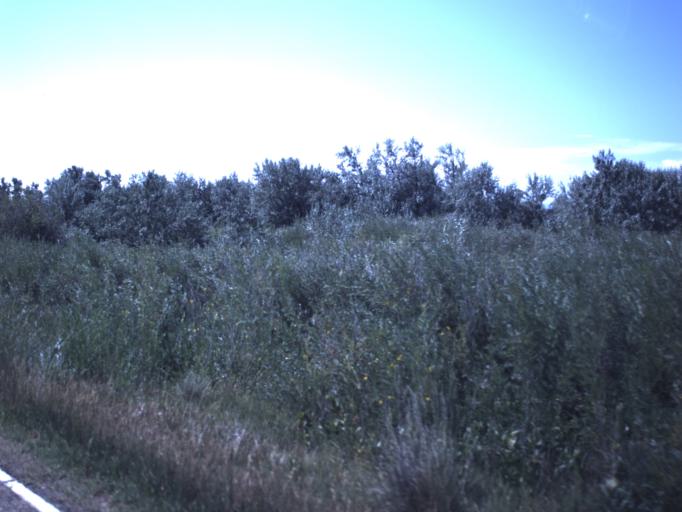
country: US
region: Utah
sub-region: Duchesne County
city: Duchesne
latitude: 40.3329
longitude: -110.2730
